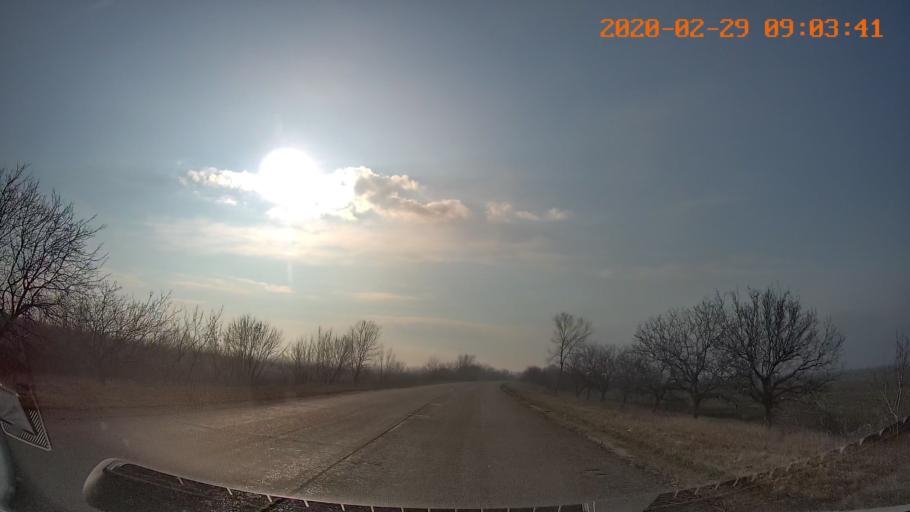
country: UA
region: Odessa
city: Velykoploske
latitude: 46.9131
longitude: 29.7321
